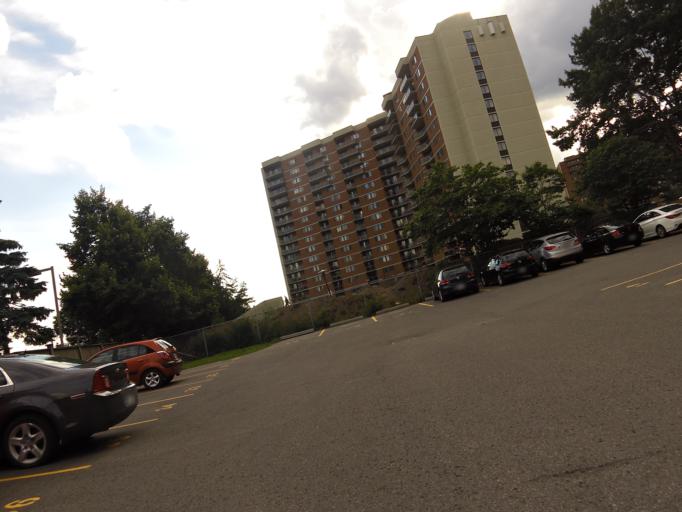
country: CA
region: Ontario
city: Bells Corners
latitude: 45.3426
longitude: -75.7862
